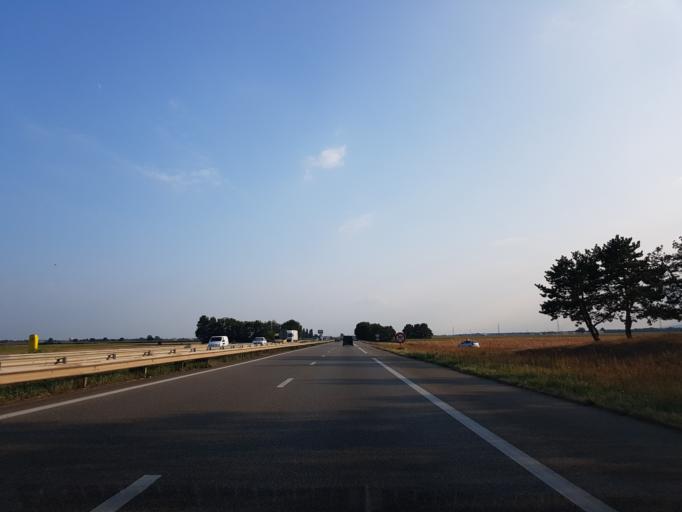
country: FR
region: Alsace
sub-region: Departement du Haut-Rhin
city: Sainte-Croix-en-Plaine
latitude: 47.9911
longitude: 7.3781
